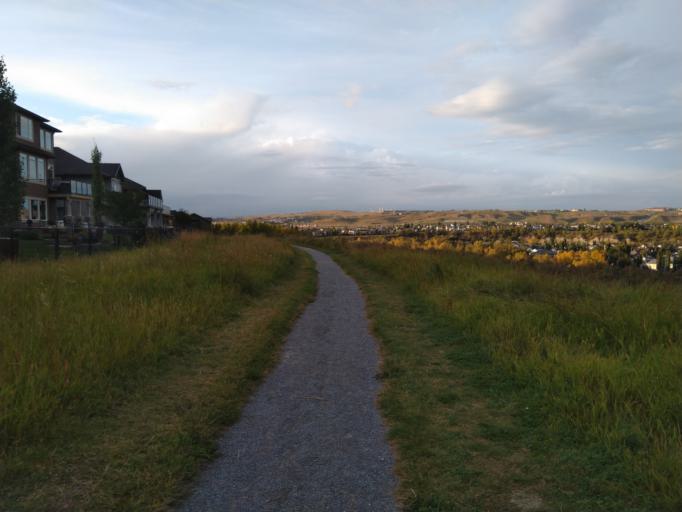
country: CA
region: Alberta
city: Cochrane
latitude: 51.1821
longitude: -114.5018
